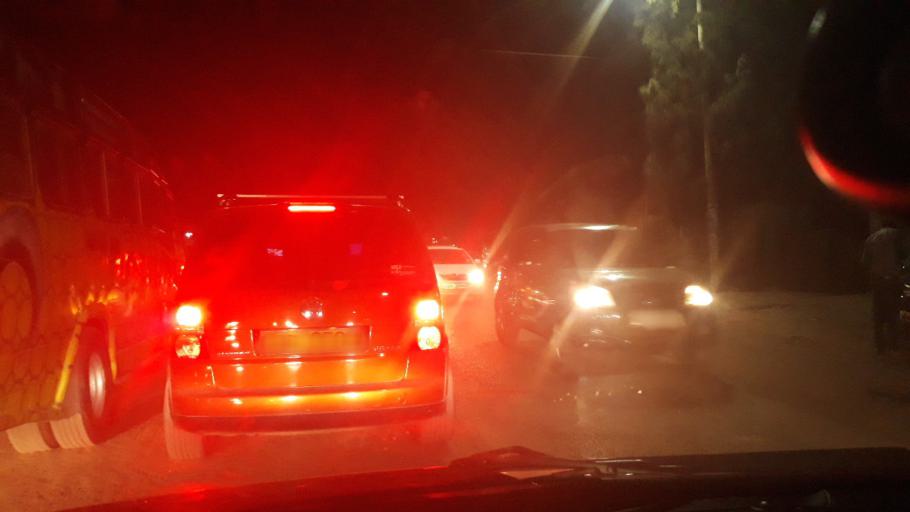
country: KE
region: Nairobi Area
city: Pumwani
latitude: -1.2758
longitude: 36.8877
